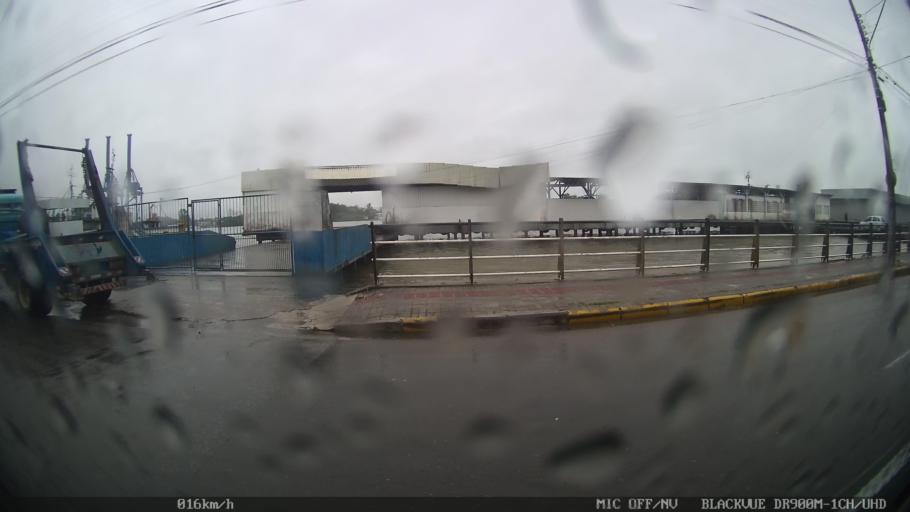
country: BR
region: Santa Catarina
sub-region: Navegantes
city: Navegantes
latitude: -26.9026
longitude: -48.6579
